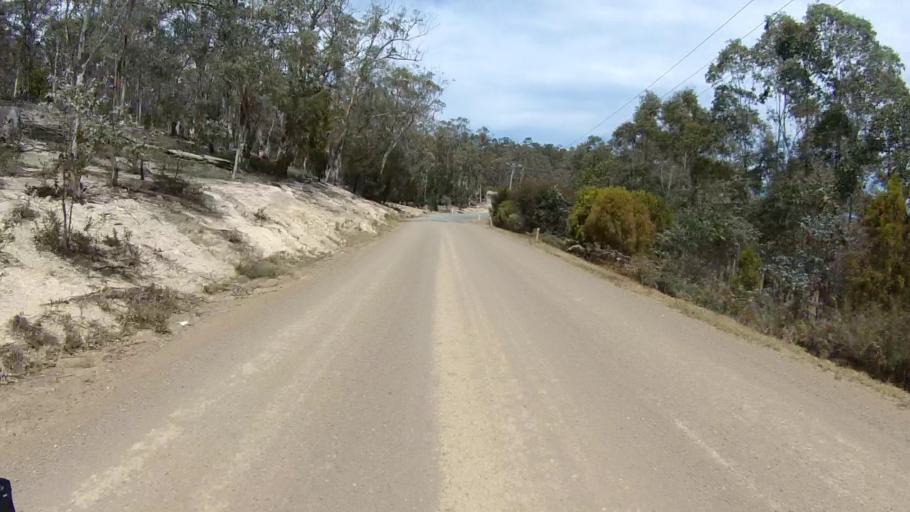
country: AU
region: Tasmania
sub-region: Sorell
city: Sorell
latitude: -42.7995
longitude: 147.6815
